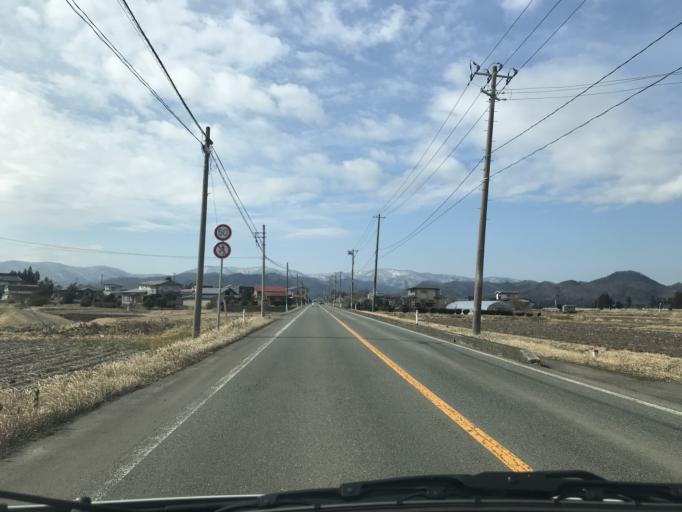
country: JP
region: Iwate
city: Hanamaki
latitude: 39.3857
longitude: 141.0648
